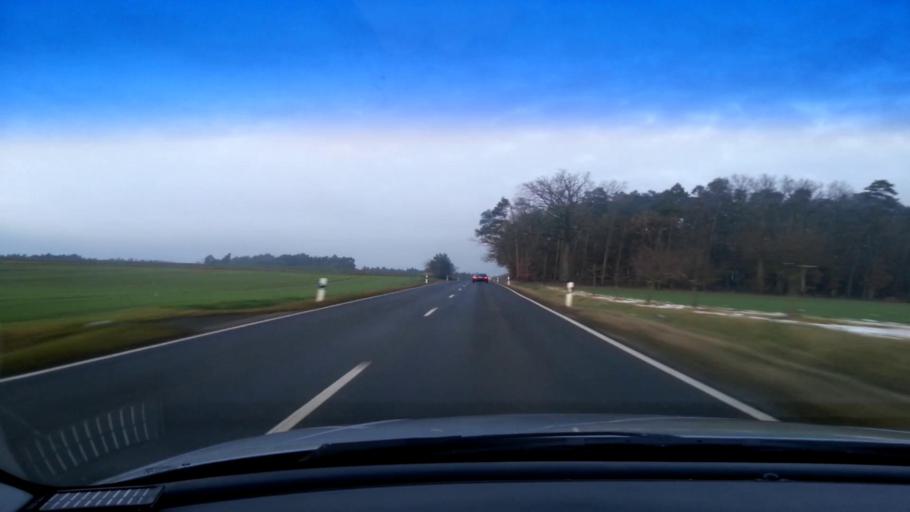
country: DE
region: Bavaria
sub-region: Upper Franconia
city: Pommersfelden
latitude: 49.7932
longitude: 10.8262
